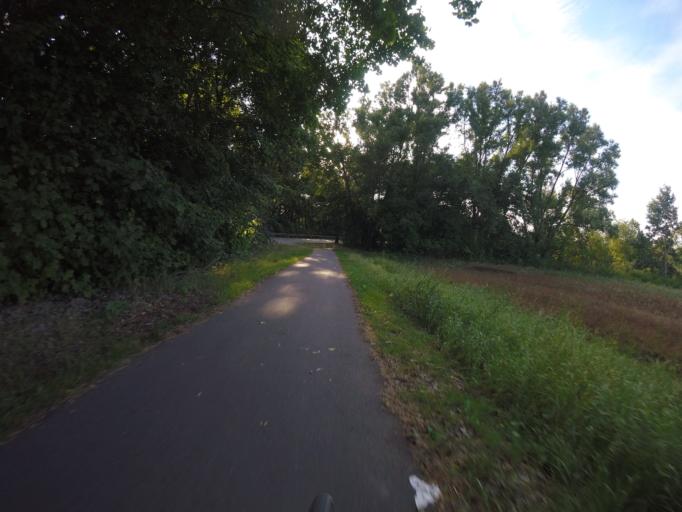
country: DE
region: Brandenburg
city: Altlandsberg
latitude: 52.5627
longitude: 13.7559
